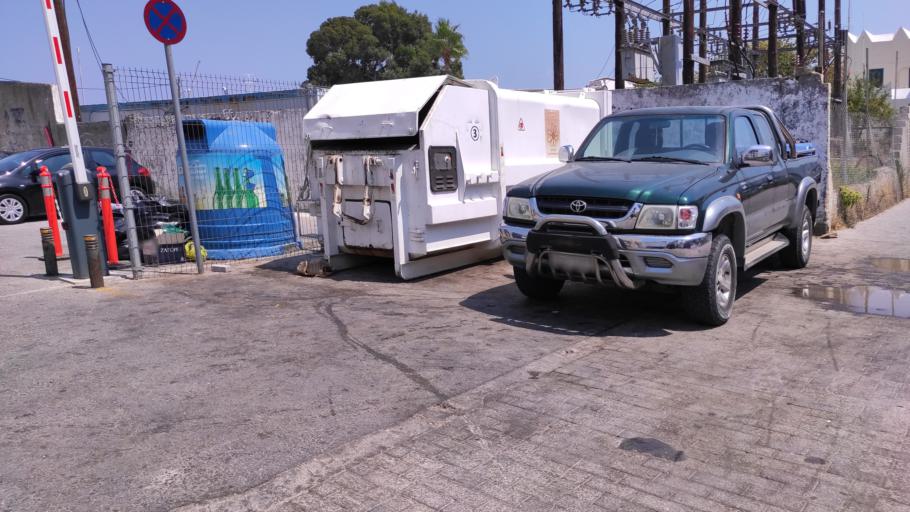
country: GR
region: South Aegean
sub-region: Nomos Dodekanisou
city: Kos
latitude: 36.8978
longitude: 27.2873
